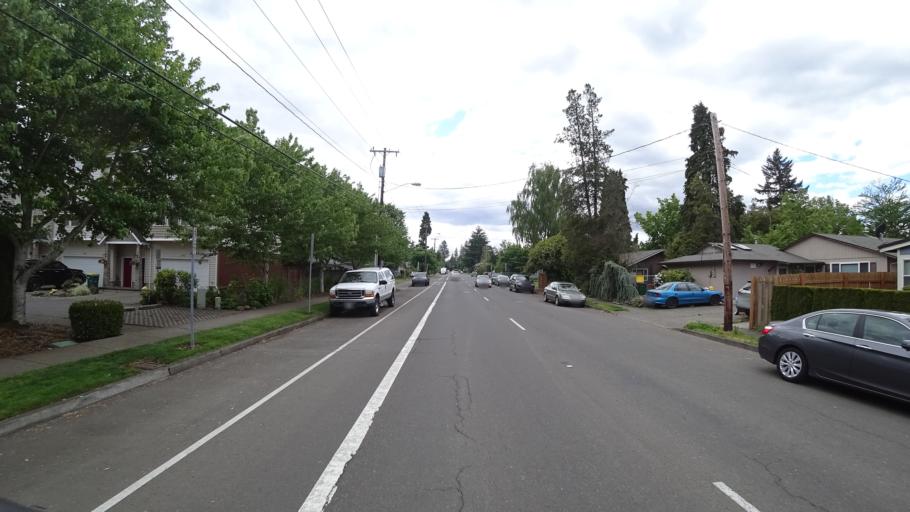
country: US
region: Oregon
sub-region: Washington County
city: Beaverton
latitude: 45.4827
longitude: -122.8049
